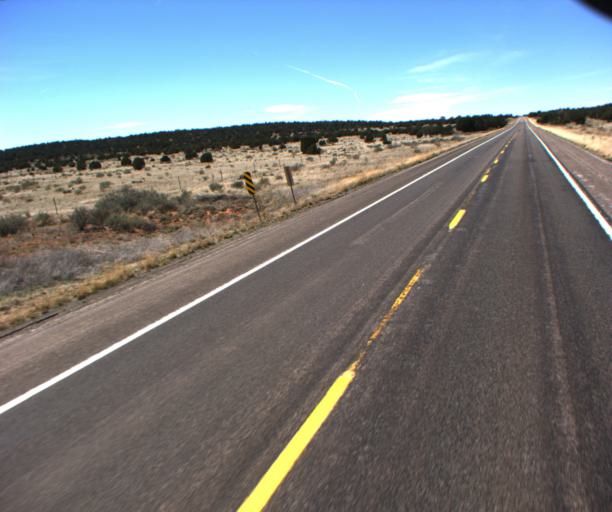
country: US
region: Arizona
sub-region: Mohave County
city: Peach Springs
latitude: 35.5047
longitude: -113.1790
